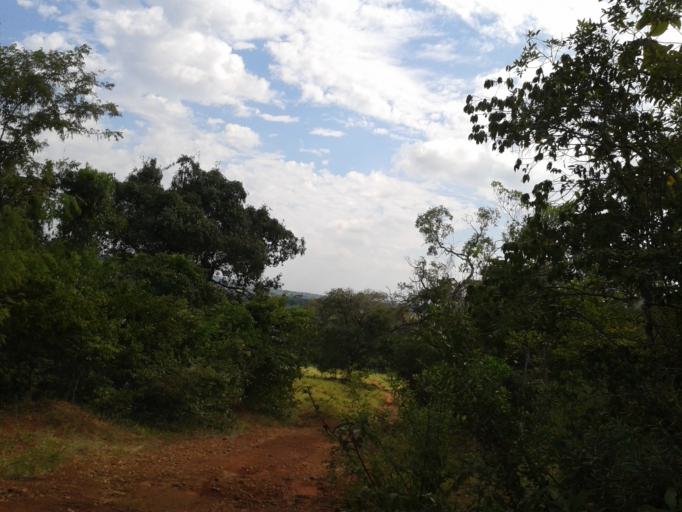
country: BR
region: Minas Gerais
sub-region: Campina Verde
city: Campina Verde
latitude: -19.3943
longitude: -49.6631
